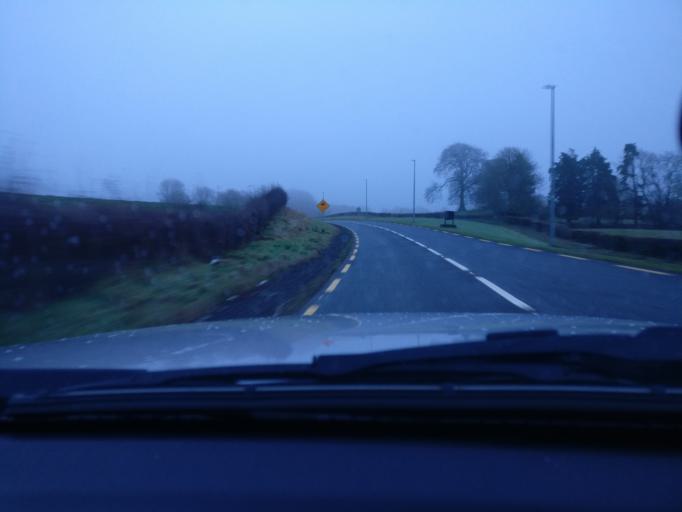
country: IE
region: Leinster
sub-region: An Iarmhi
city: Rathwire
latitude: 53.6125
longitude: -7.0753
